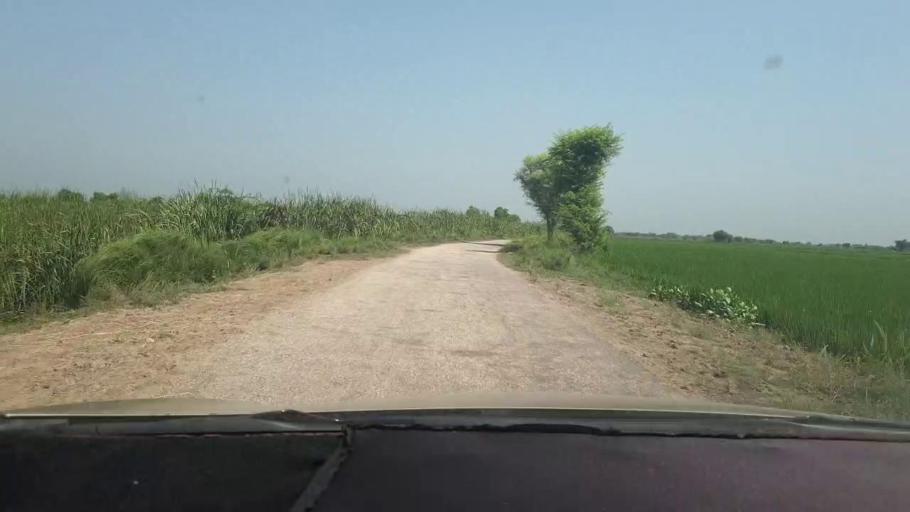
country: PK
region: Sindh
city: Miro Khan
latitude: 27.7013
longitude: 68.0903
